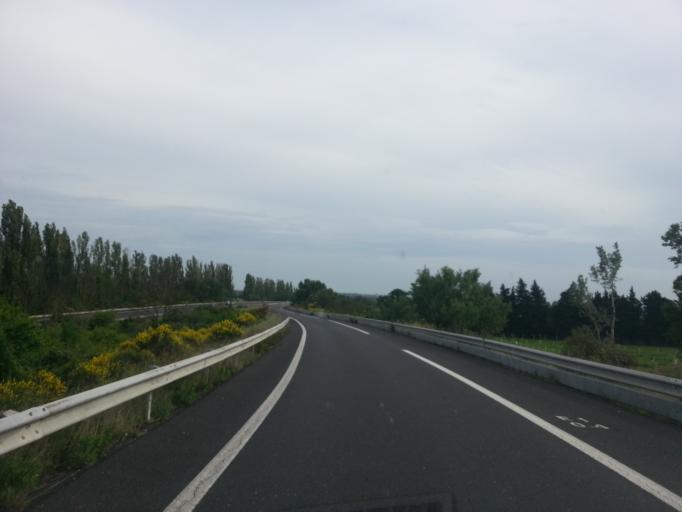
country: FR
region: Provence-Alpes-Cote d'Azur
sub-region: Departement du Vaucluse
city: Orange
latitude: 44.1283
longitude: 4.7893
